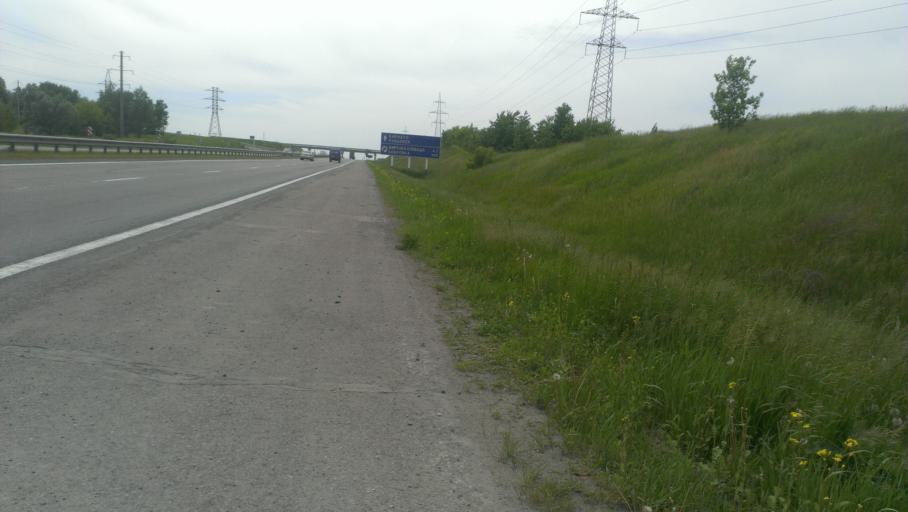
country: RU
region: Altai Krai
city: Sannikovo
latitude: 53.3446
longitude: 83.9416
